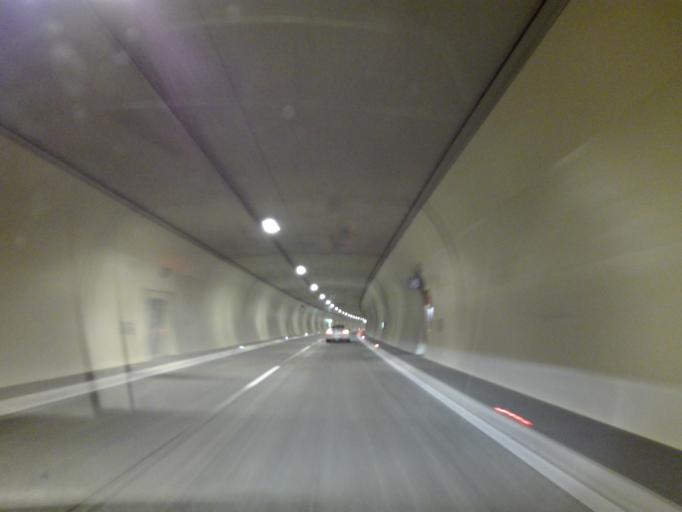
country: AT
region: Upper Austria
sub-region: Politischer Bezirk Urfahr-Umgebung
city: Alberndorf in der Riedmark
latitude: 48.4080
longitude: 14.4830
